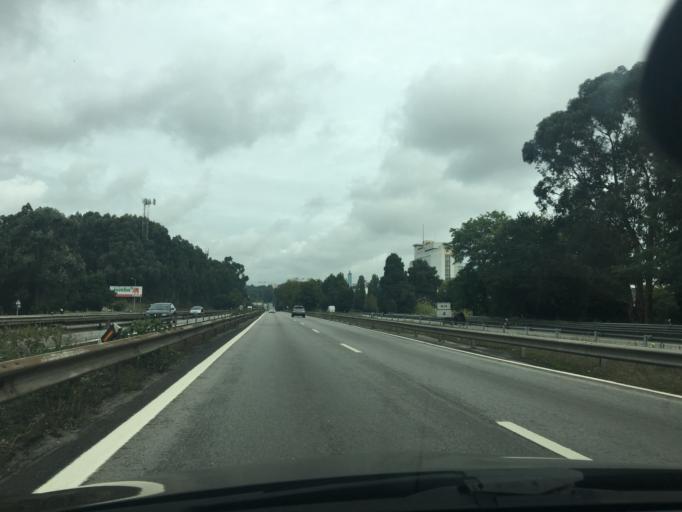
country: PT
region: Porto
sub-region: Maia
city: Leca do Bailio
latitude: 41.2090
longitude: -8.6272
